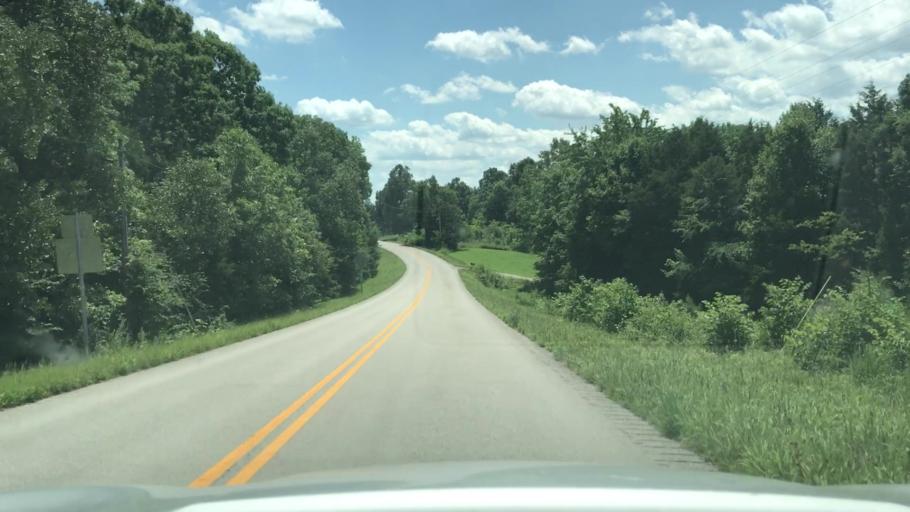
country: US
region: Kentucky
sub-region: Hopkins County
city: Nortonville
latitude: 37.1001
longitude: -87.3407
